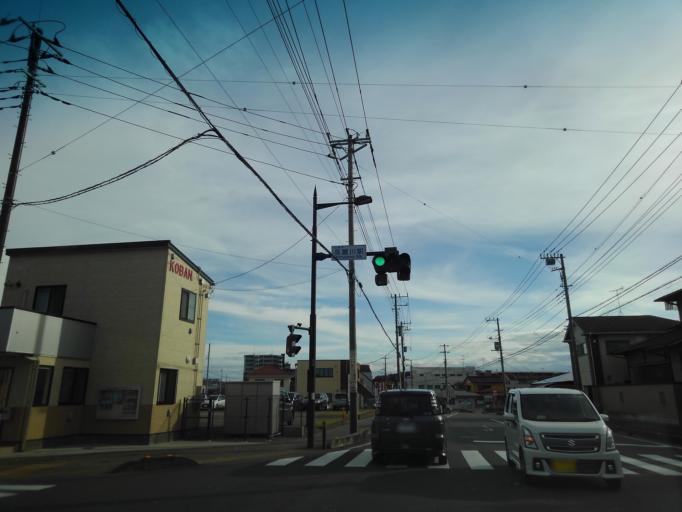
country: JP
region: Saitama
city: Hanno
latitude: 35.8958
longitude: 139.3367
